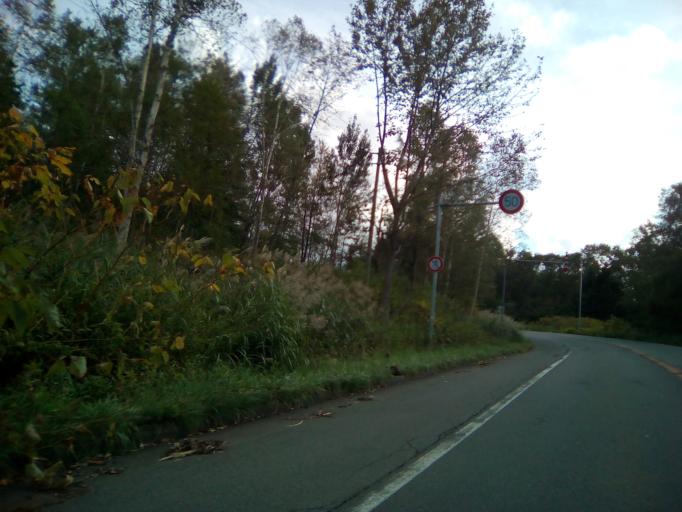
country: JP
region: Hokkaido
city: Niseko Town
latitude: 42.6806
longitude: 140.8366
